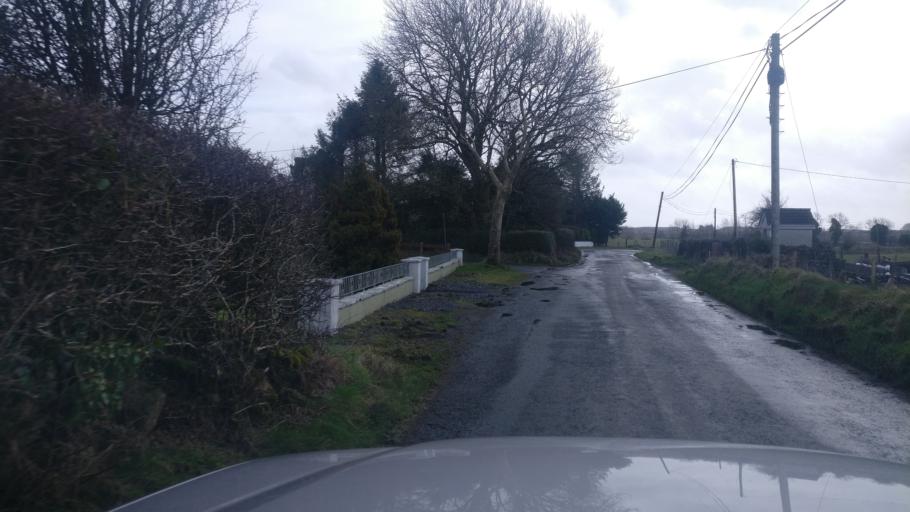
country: IE
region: Connaught
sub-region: County Galway
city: Loughrea
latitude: 53.2912
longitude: -8.4771
